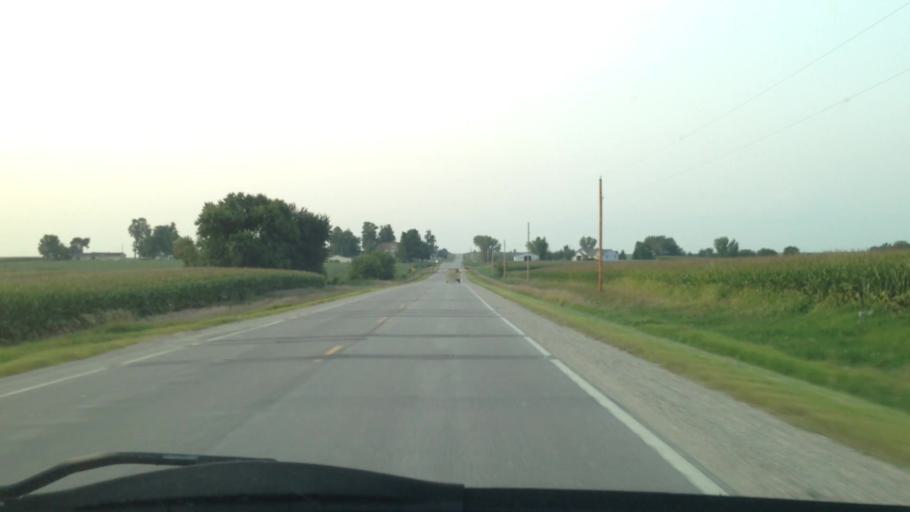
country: US
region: Iowa
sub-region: Benton County
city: Atkins
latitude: 42.0021
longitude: -91.8735
